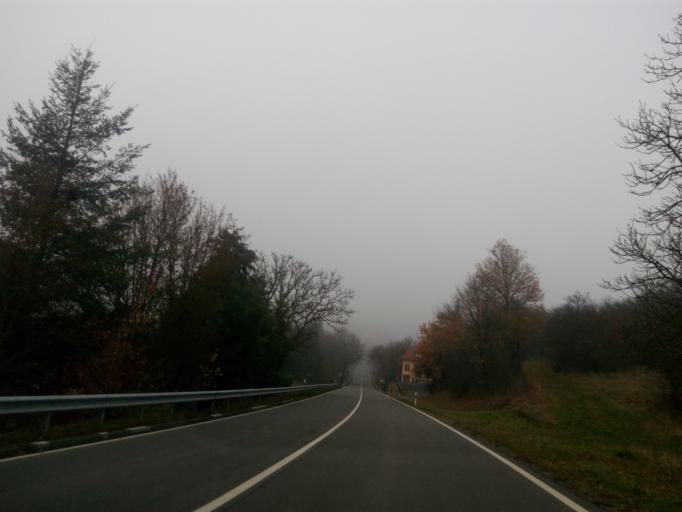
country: DE
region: Rheinland-Pfalz
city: Sienhachenbach
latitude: 49.6991
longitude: 7.4856
